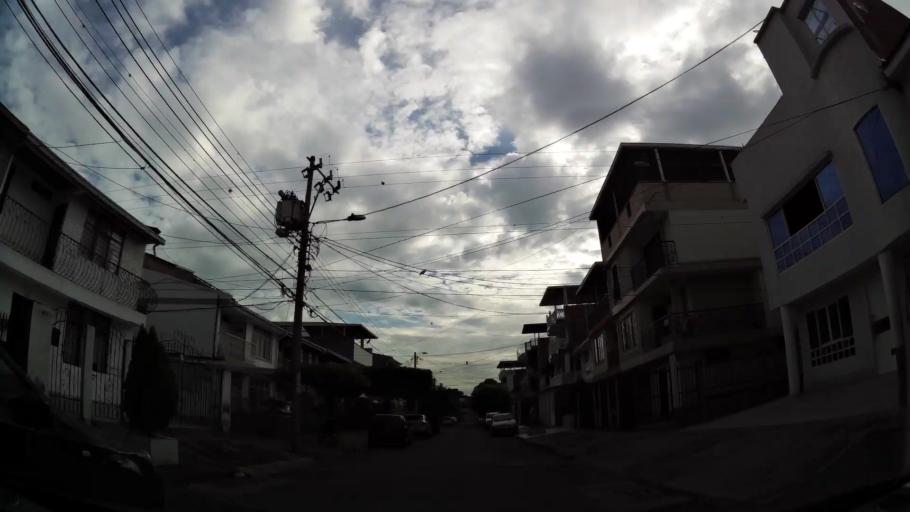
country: CO
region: Valle del Cauca
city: Cali
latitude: 3.4691
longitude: -76.4969
